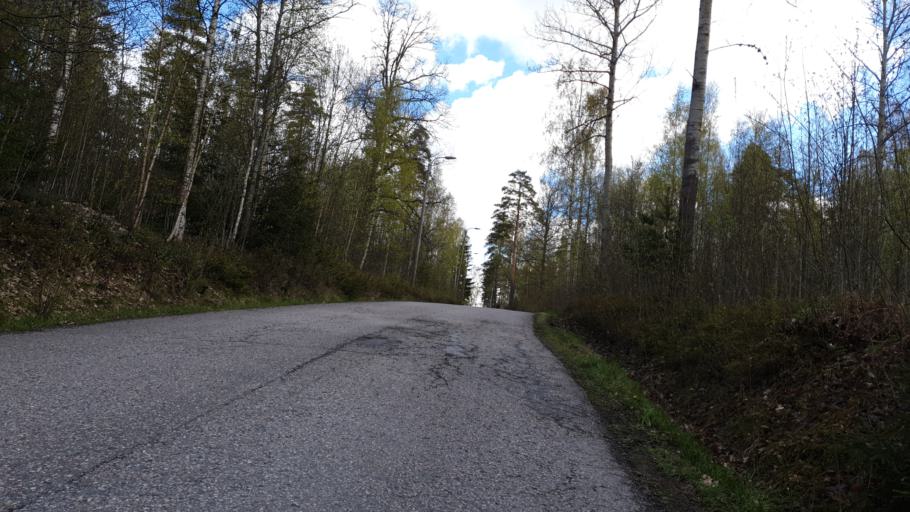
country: FI
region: Uusimaa
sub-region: Helsinki
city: Nurmijaervi
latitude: 60.3467
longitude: 24.8407
